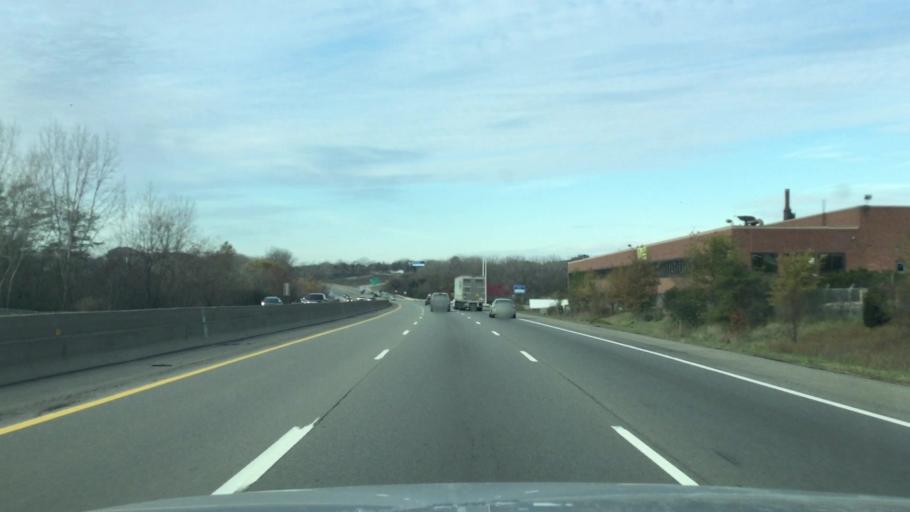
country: US
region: Michigan
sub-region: Washtenaw County
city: Ypsilanti
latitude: 42.2316
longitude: -83.6019
